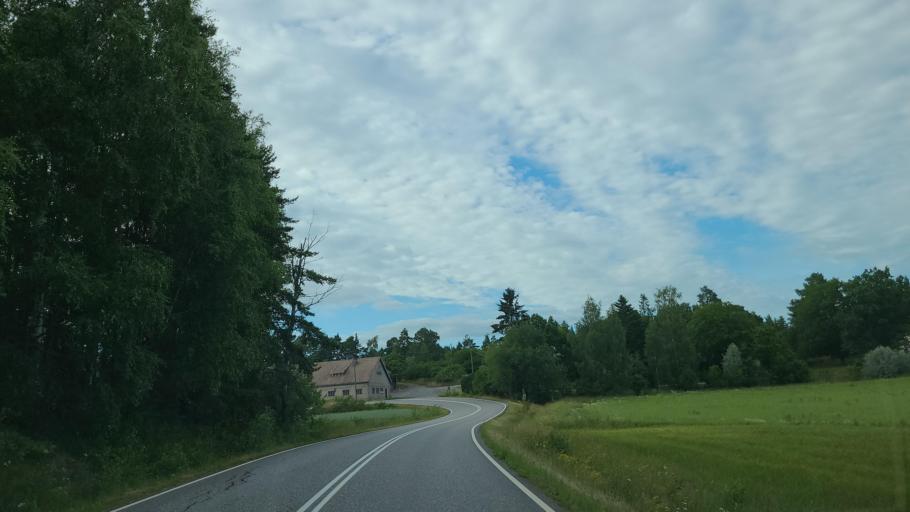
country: FI
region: Varsinais-Suomi
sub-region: Turku
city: Rymaettylae
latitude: 60.3526
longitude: 21.9586
